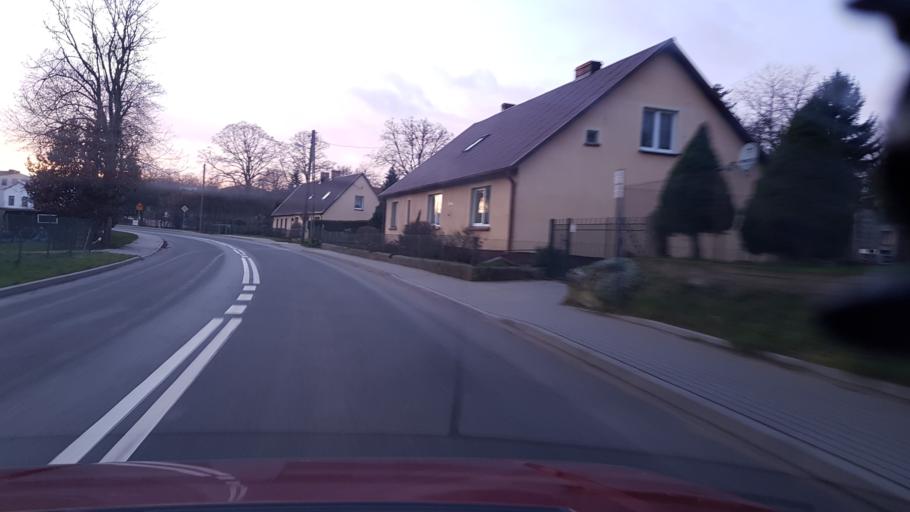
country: PL
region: Pomeranian Voivodeship
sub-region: Powiat bytowski
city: Bytow
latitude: 54.1368
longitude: 17.4246
